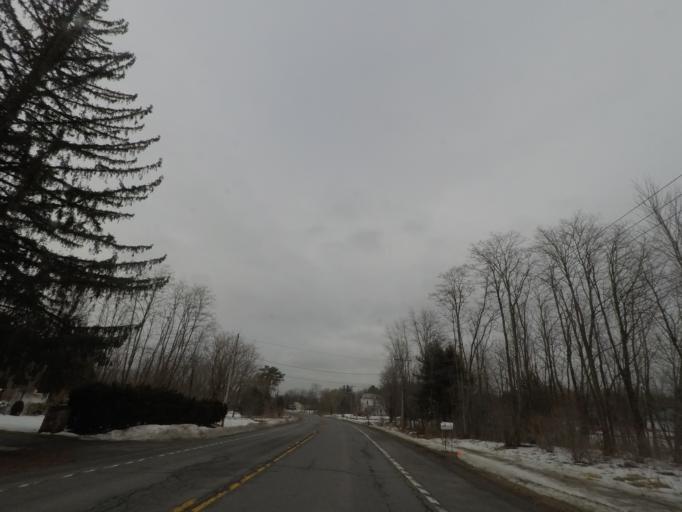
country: US
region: New York
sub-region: Schenectady County
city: Rotterdam
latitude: 42.7512
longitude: -73.9843
